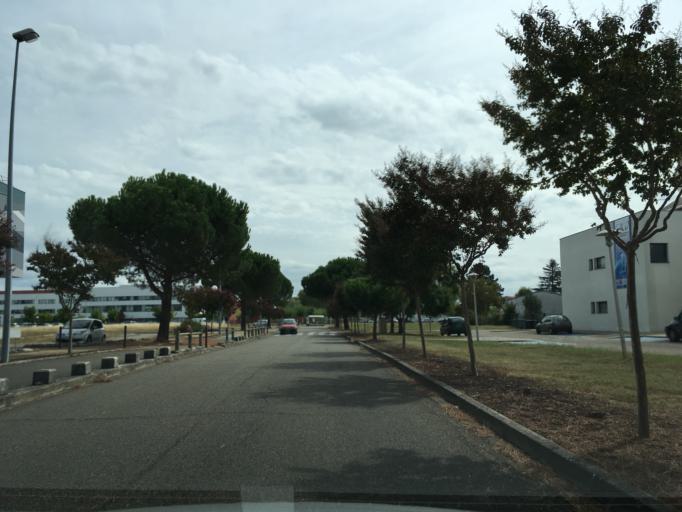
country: FR
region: Aquitaine
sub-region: Departement du Lot-et-Garonne
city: Agen
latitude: 44.1857
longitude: 0.6252
